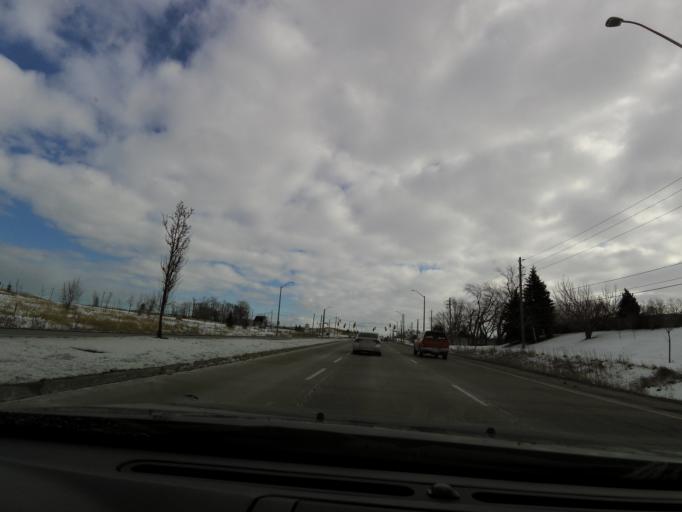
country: CA
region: Ontario
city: Hamilton
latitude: 43.1932
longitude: -79.7816
